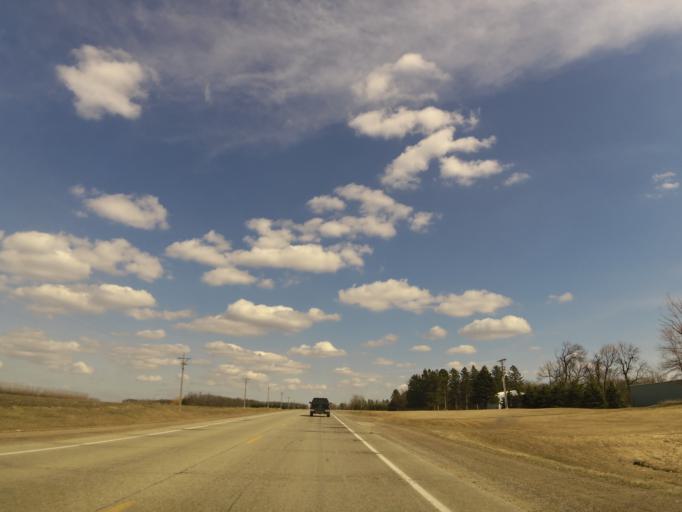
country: US
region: South Dakota
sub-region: Codington County
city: Watertown
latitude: 44.8901
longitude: -96.9488
